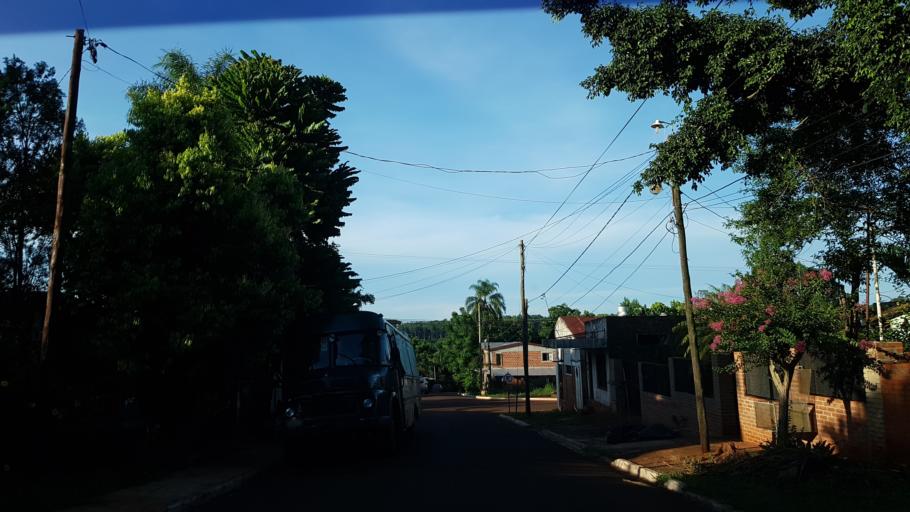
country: AR
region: Misiones
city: Puerto Libertad
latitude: -25.9216
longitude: -54.5831
